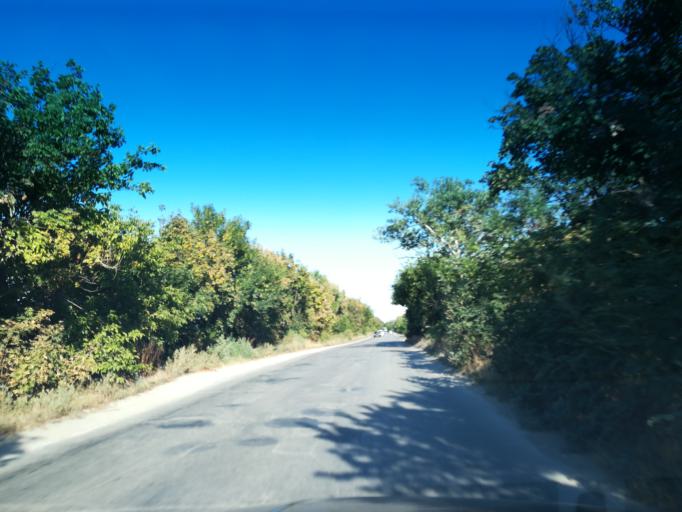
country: BG
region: Plovdiv
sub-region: Obshtina Plovdiv
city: Plovdiv
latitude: 42.1655
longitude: 24.7983
